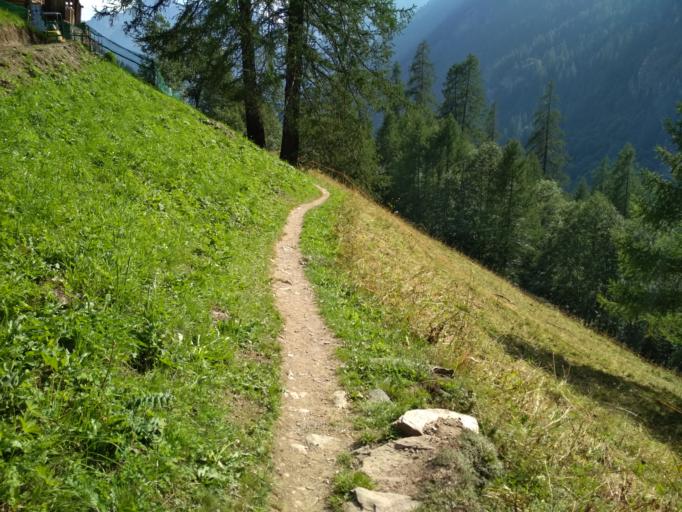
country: IT
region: Aosta Valley
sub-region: Valle d'Aosta
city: Gressoney-La-Trinite
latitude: 45.8046
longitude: 7.8268
